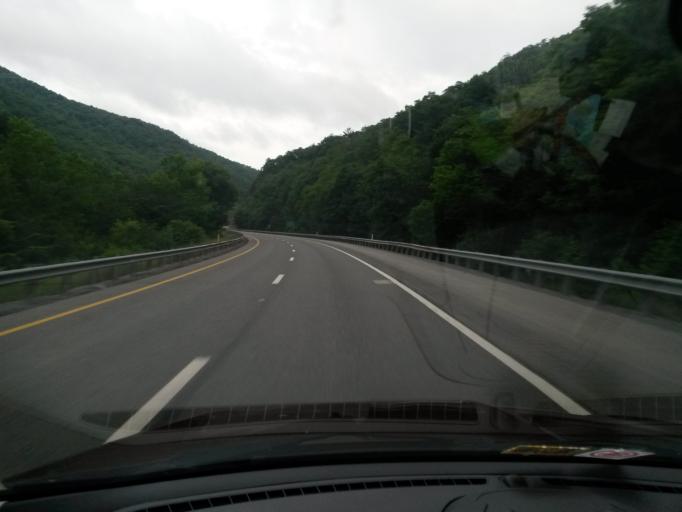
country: US
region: West Virginia
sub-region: Greenbrier County
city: White Sulphur Springs
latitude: 37.7889
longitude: -80.2526
